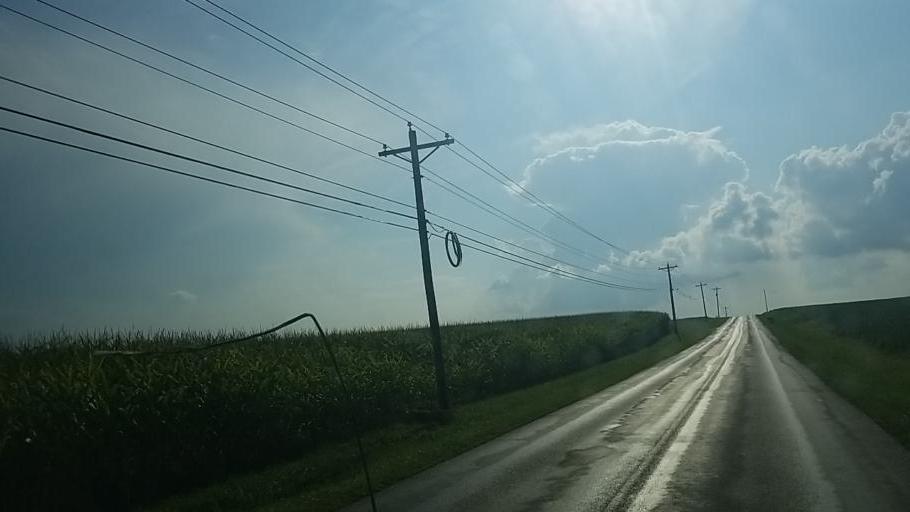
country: US
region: Ohio
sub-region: Wayne County
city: Wooster
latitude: 40.8582
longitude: -81.9858
